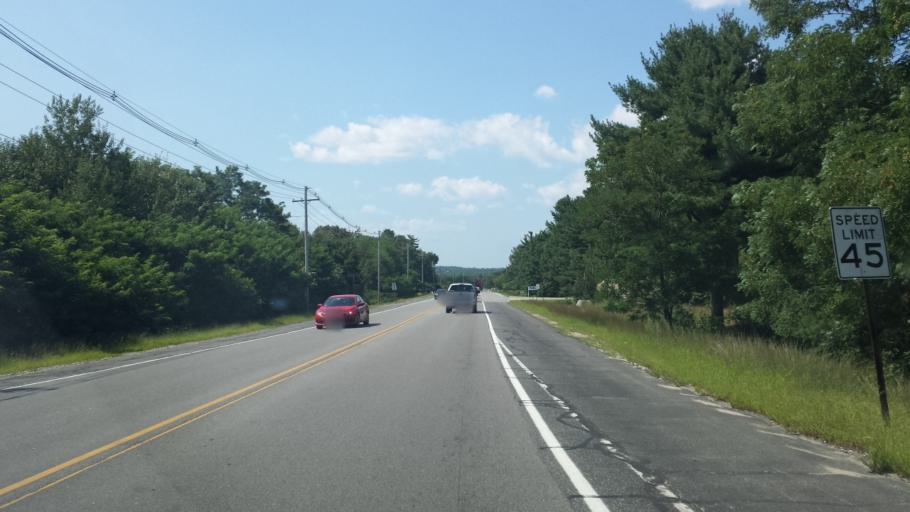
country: US
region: Maine
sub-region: York County
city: Biddeford
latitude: 43.4699
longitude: -70.4858
